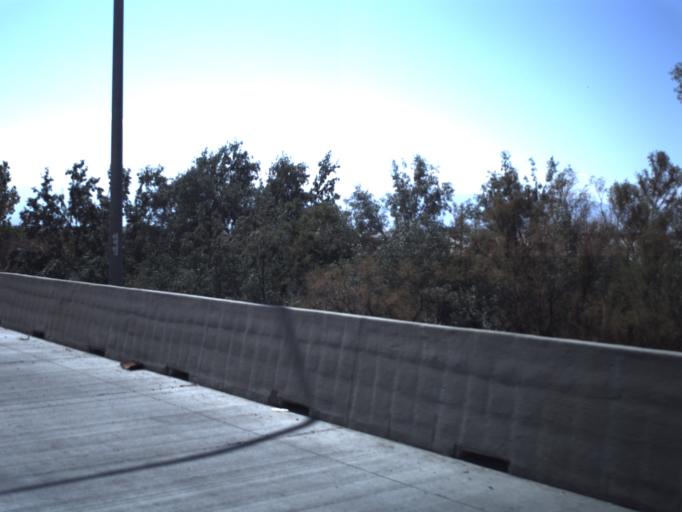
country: US
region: Utah
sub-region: Tooele County
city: Stansbury park
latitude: 40.7011
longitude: -112.2582
